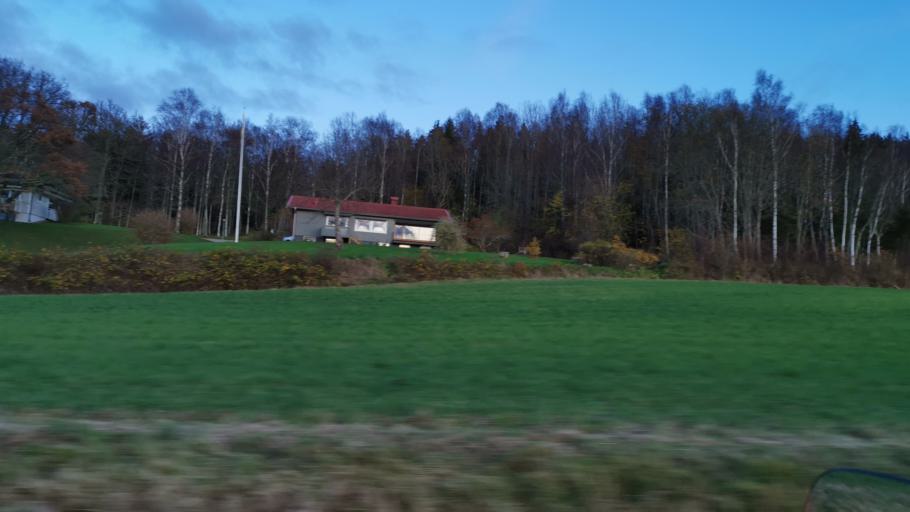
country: SE
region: Vaestra Goetaland
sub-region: Munkedals Kommun
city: Munkedal
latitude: 58.3875
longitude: 11.6629
